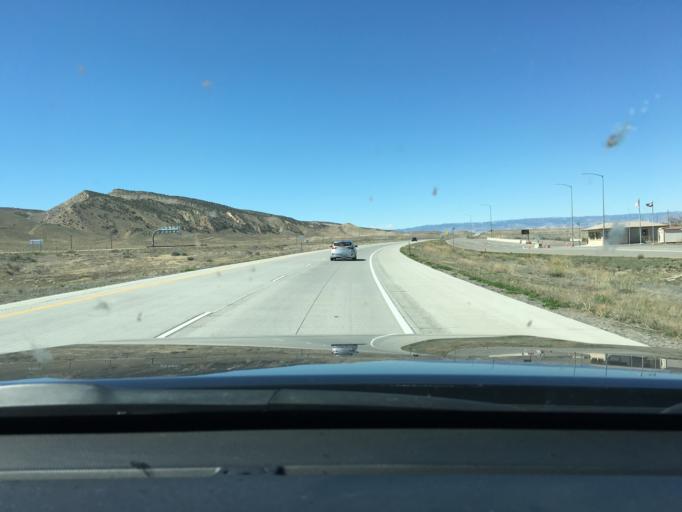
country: US
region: Colorado
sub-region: Mesa County
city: Loma
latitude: 39.1800
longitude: -108.8242
